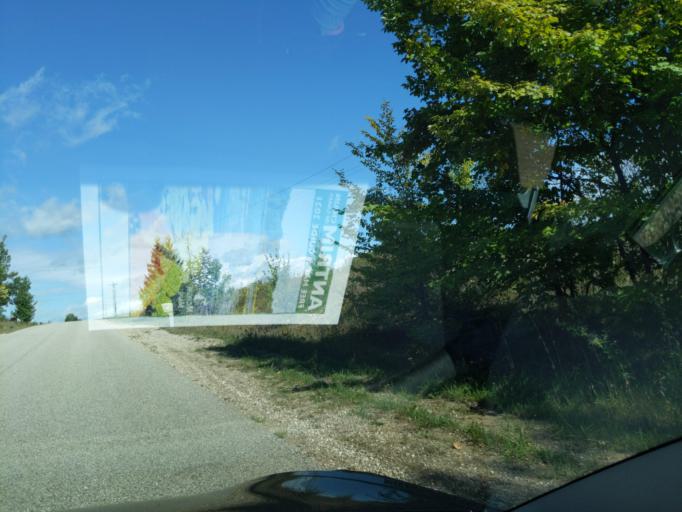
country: US
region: Michigan
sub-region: Antrim County
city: Elk Rapids
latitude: 44.9496
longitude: -85.3324
